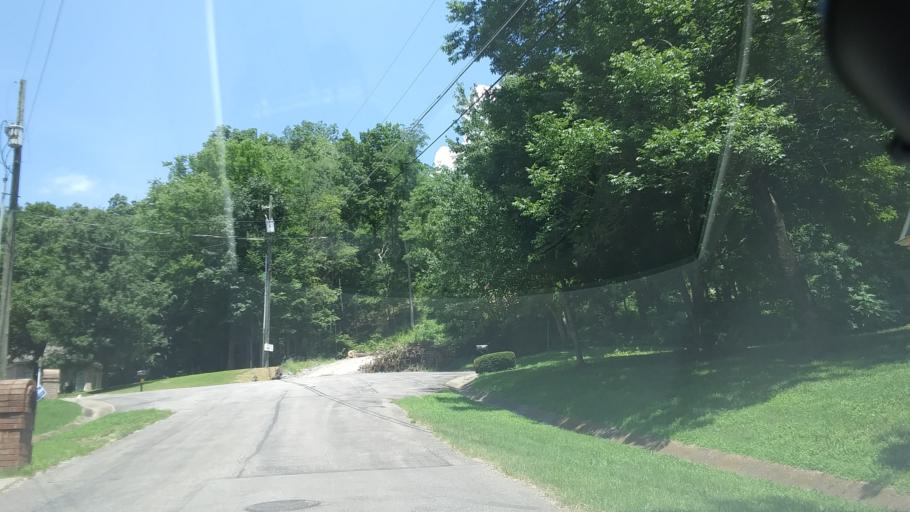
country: US
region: Tennessee
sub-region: Davidson County
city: Belle Meade
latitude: 36.0903
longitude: -86.9488
